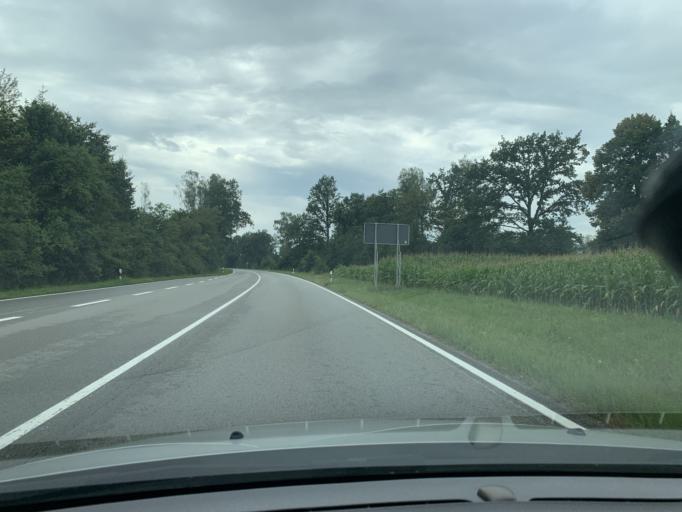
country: DE
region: Bavaria
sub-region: Upper Bavaria
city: Mettenheim
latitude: 48.2497
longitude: 12.4710
